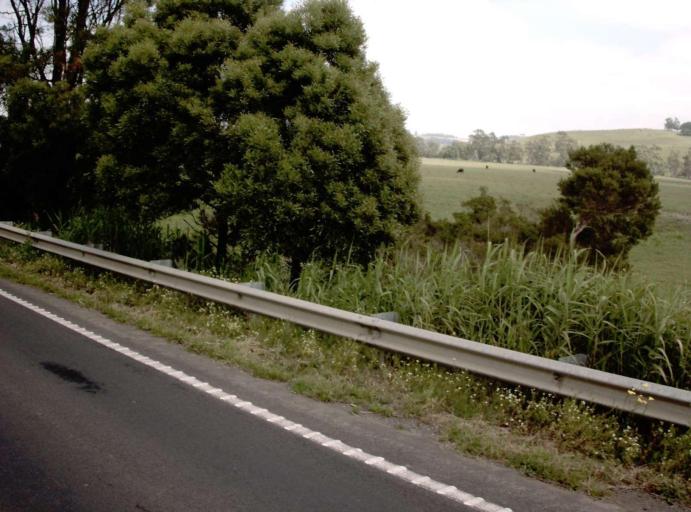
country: AU
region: Victoria
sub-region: Baw Baw
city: Warragul
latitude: -38.4445
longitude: 146.0279
